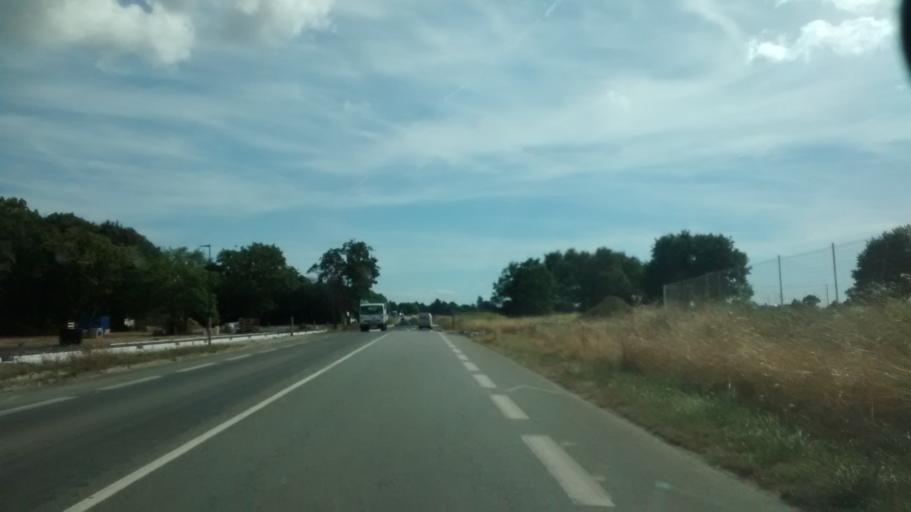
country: FR
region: Pays de la Loire
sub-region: Departement de la Loire-Atlantique
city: Pont-Saint-Martin
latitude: 47.1507
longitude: -1.6010
